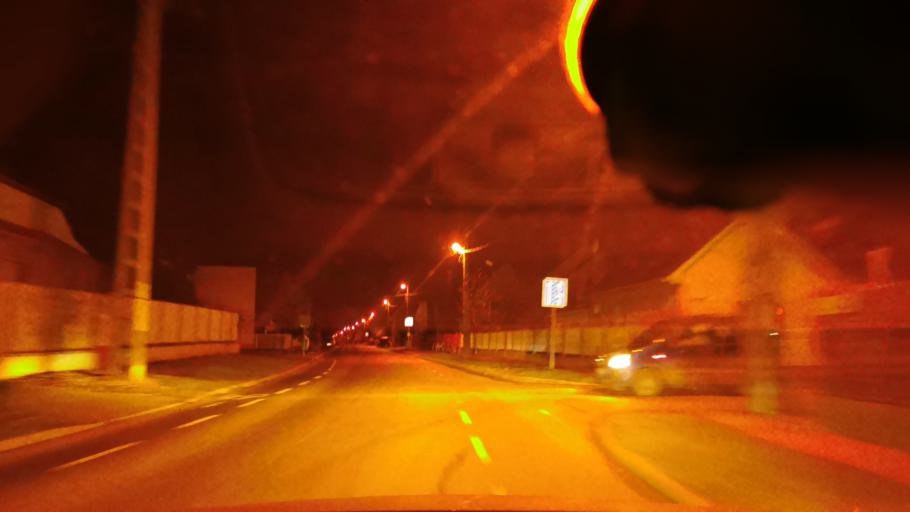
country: HU
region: Hajdu-Bihar
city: Debrecen
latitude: 47.5922
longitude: 21.5715
